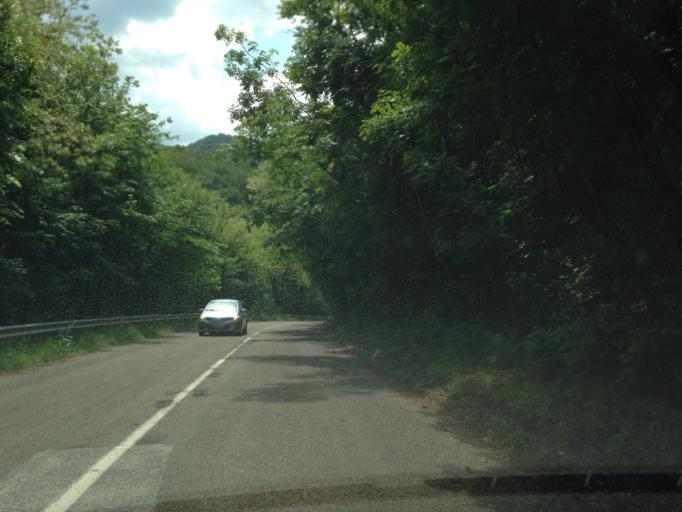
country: HU
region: Pest
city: Visegrad
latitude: 47.7602
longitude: 18.9548
